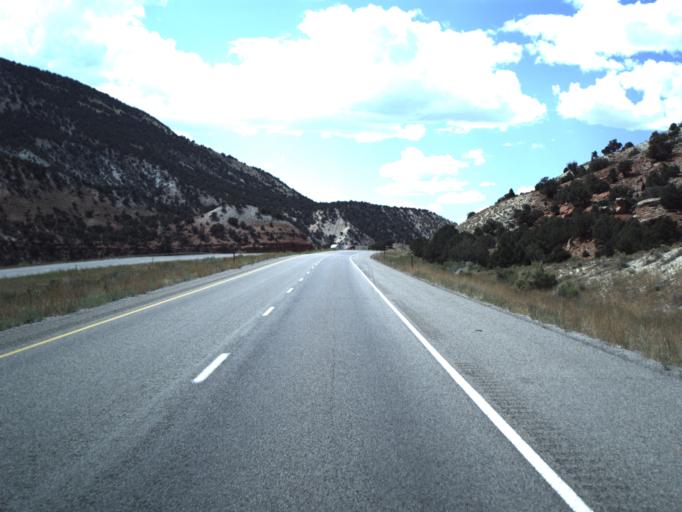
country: US
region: Utah
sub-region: Sevier County
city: Salina
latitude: 38.9255
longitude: -111.7763
